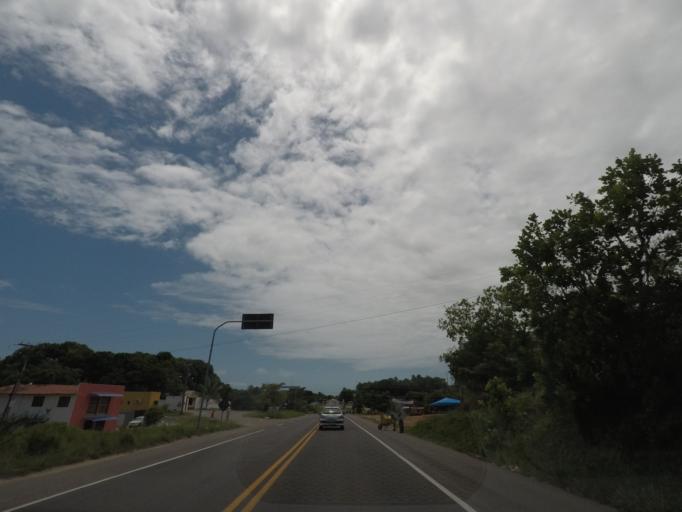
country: BR
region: Bahia
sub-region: Itaparica
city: Itaparica
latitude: -12.9516
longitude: -38.6322
